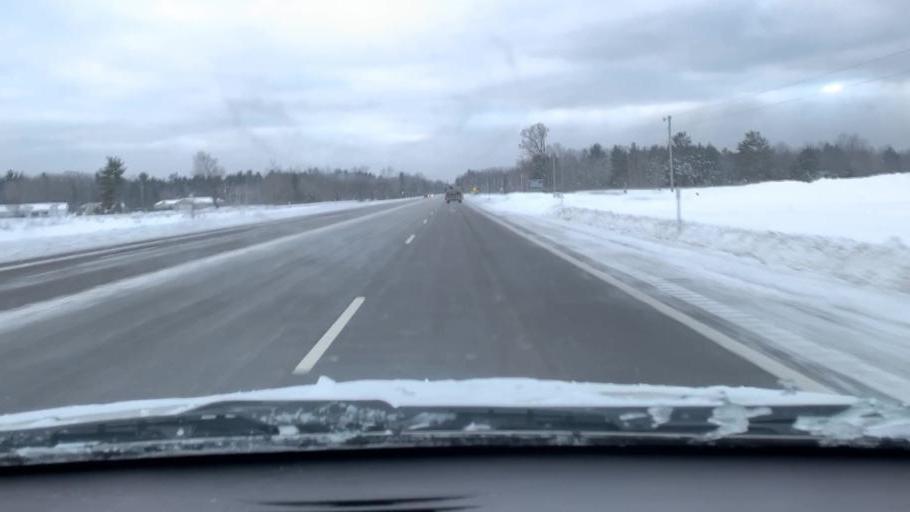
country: US
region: Michigan
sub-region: Kalkaska County
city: Kalkaska
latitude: 44.6711
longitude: -85.2396
